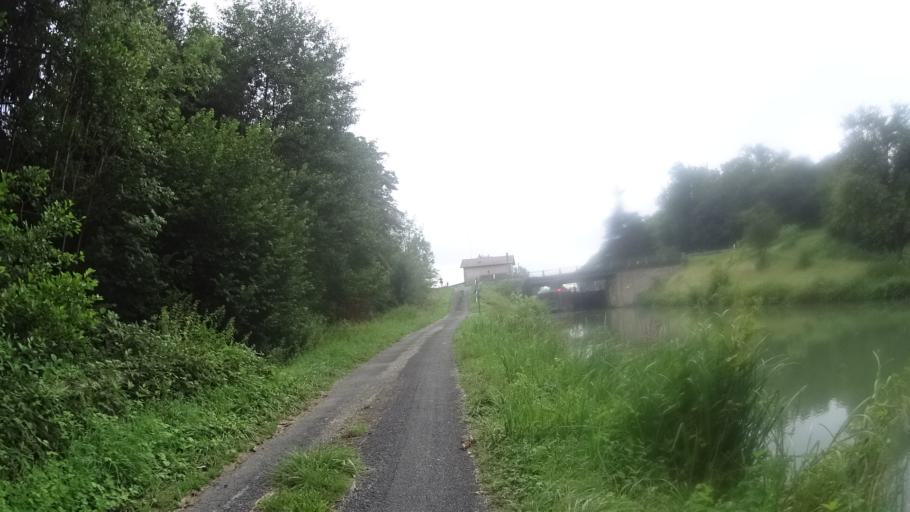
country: FR
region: Lorraine
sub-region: Departement de la Meuse
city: Fains-Veel
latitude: 48.8068
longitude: 5.0924
